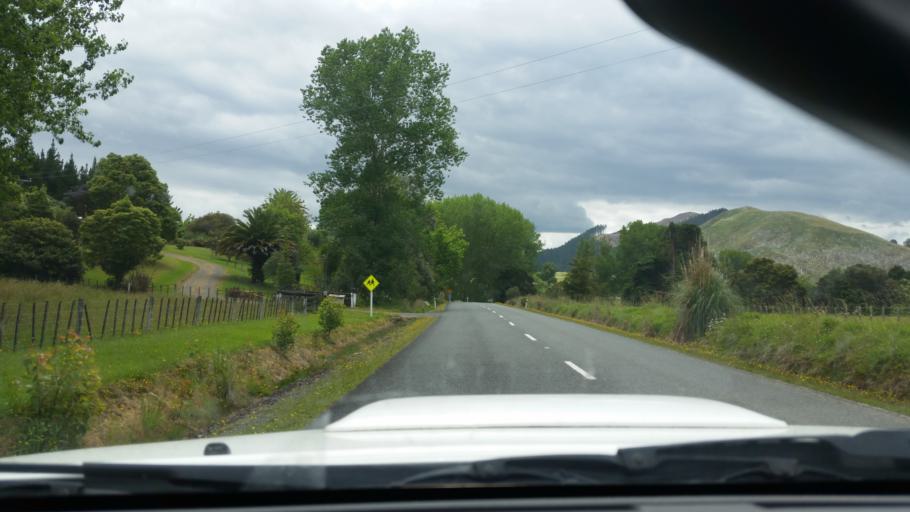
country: NZ
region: Northland
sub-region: Kaipara District
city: Dargaville
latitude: -35.7485
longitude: 173.8783
